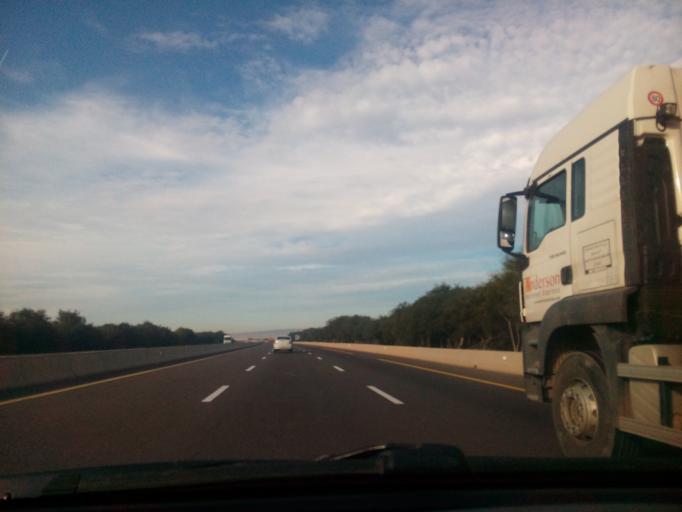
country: DZ
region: Mascara
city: Sig
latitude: 35.5836
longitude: -0.1927
